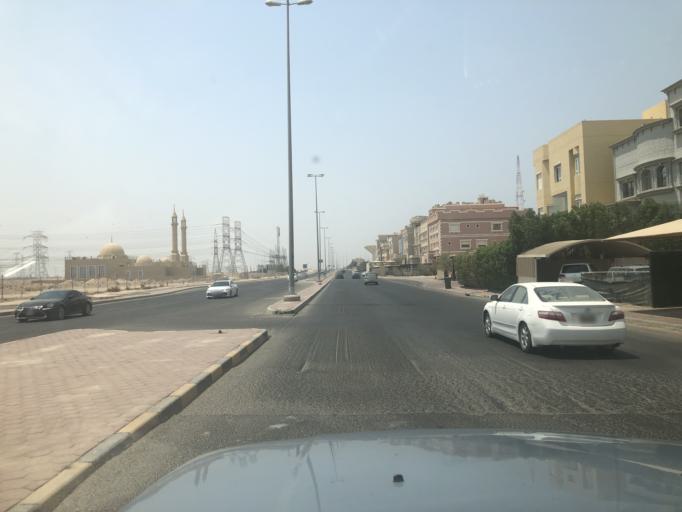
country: KW
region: Al Asimah
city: Ar Rabiyah
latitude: 29.2366
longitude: 47.8930
